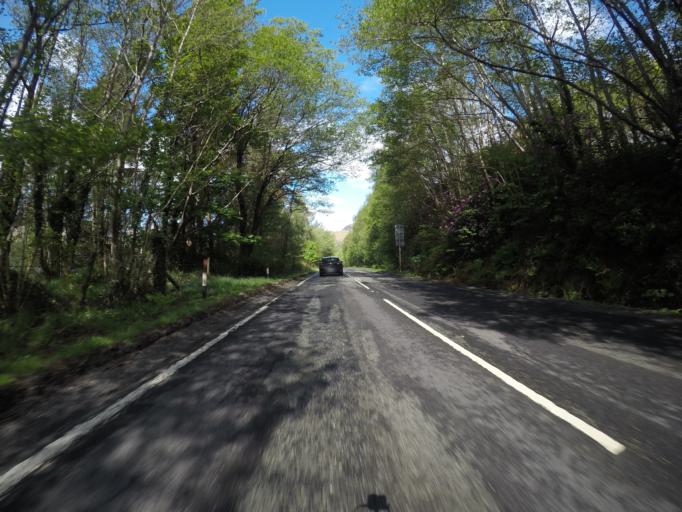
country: GB
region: Scotland
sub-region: Highland
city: Fort William
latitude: 57.2485
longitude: -5.4696
